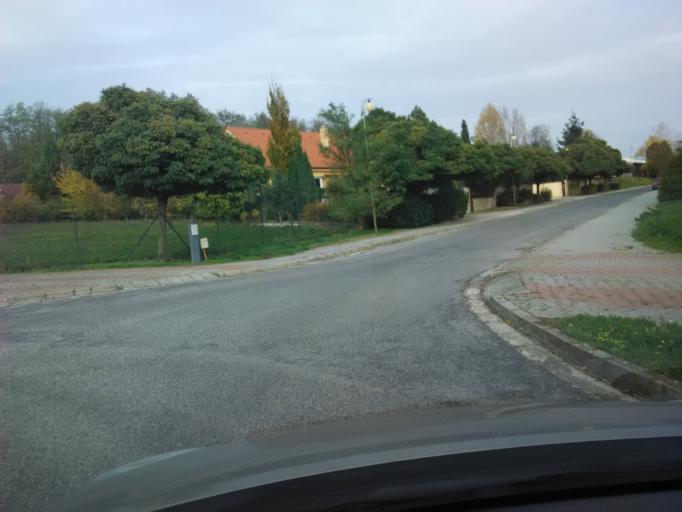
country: SK
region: Nitriansky
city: Tlmace
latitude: 48.2981
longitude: 18.5162
